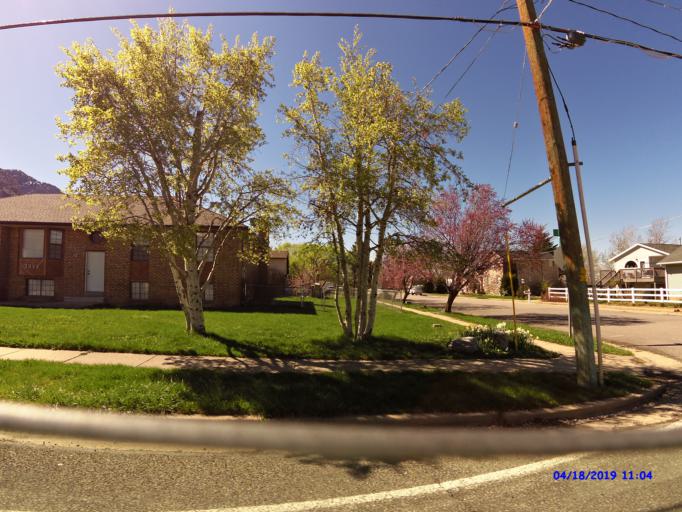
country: US
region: Utah
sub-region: Weber County
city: North Ogden
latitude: 41.2889
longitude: -111.9576
